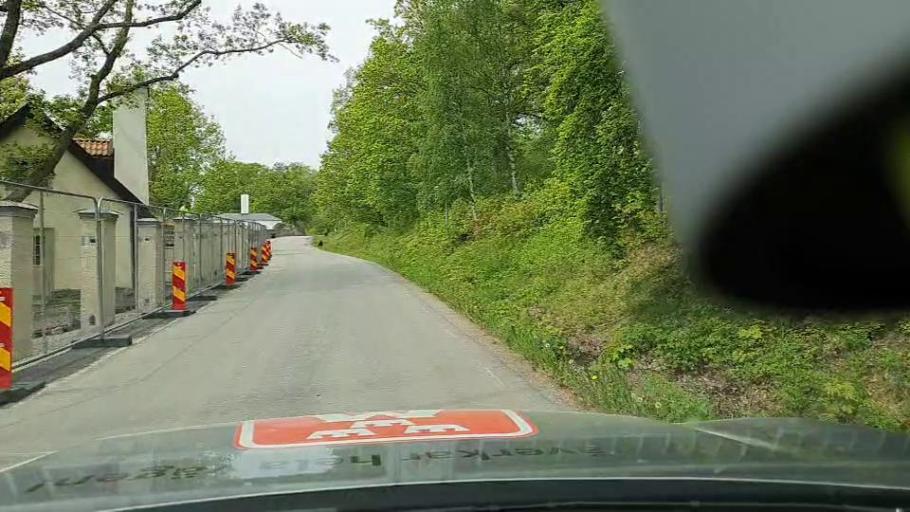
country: SE
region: Soedermanland
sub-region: Flens Kommun
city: Halleforsnas
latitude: 59.0992
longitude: 16.4865
